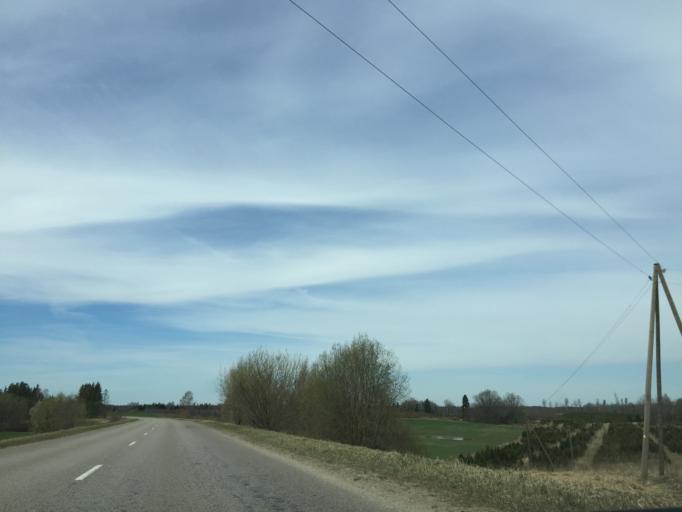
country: LV
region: Valkas Rajons
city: Valka
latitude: 57.7866
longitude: 25.9007
